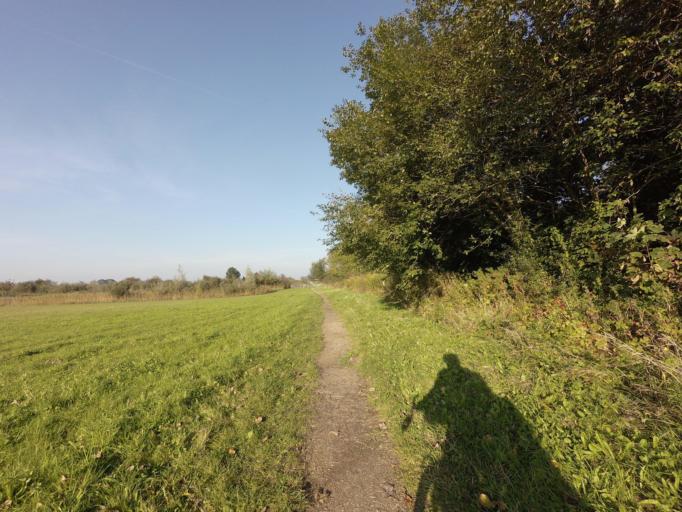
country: NL
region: Gelderland
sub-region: Gemeente Culemborg
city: Culemborg
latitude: 51.9651
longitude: 5.1774
